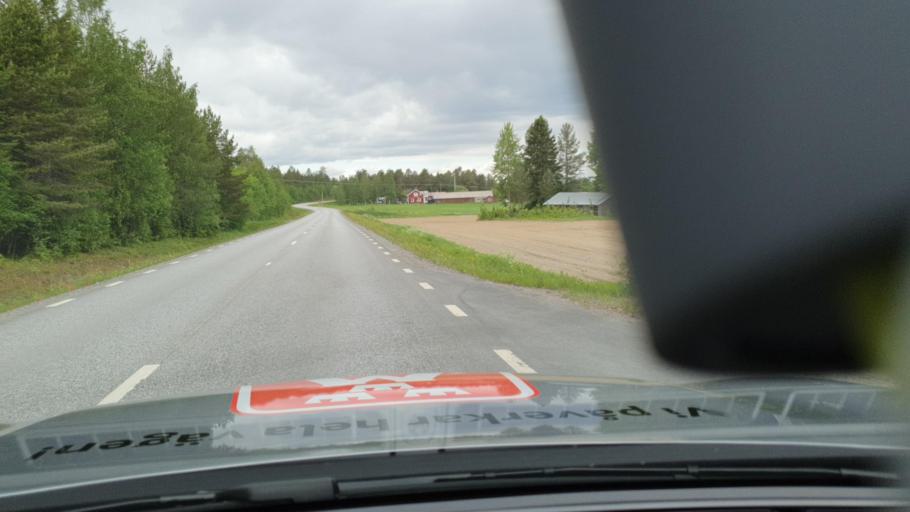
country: SE
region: Norrbotten
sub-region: Lulea Kommun
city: Lulea
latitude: 65.7327
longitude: 22.1863
